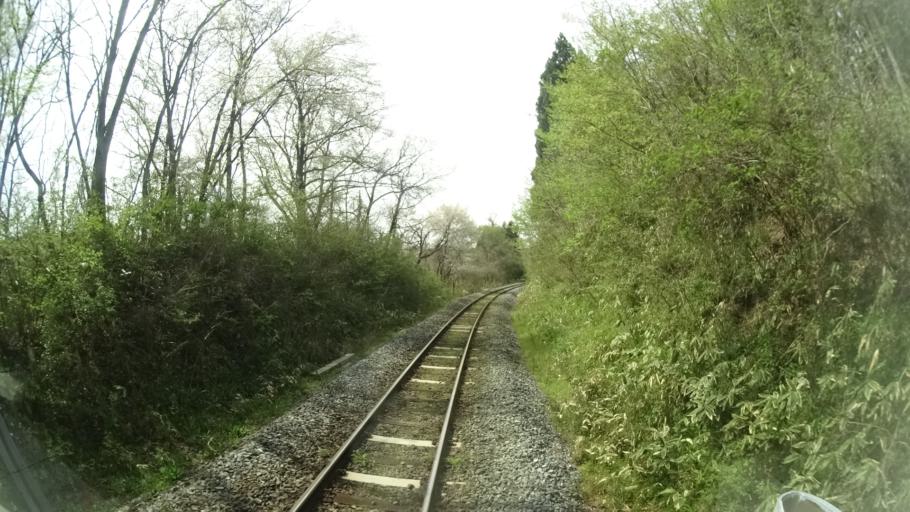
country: JP
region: Iwate
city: Ichinoseki
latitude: 38.9841
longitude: 141.3314
